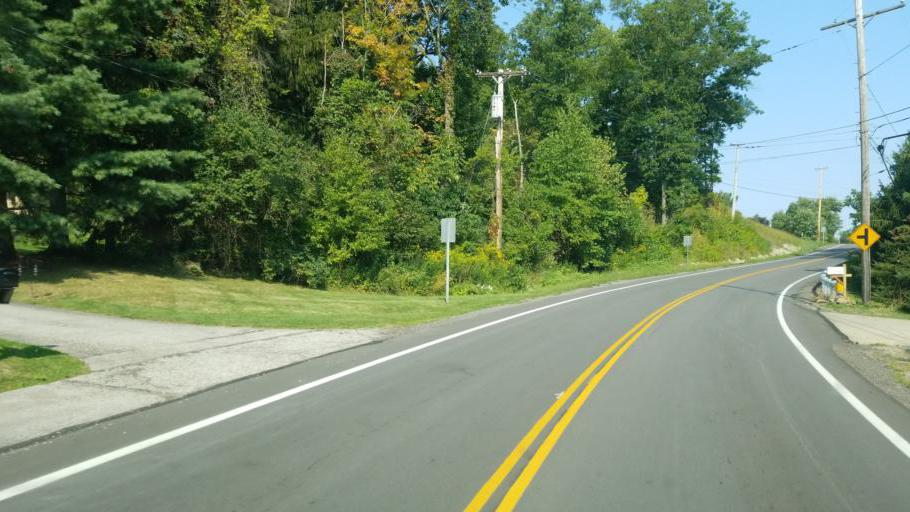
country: US
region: Ohio
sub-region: Lake County
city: Painesville
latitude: 41.6985
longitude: -81.2374
